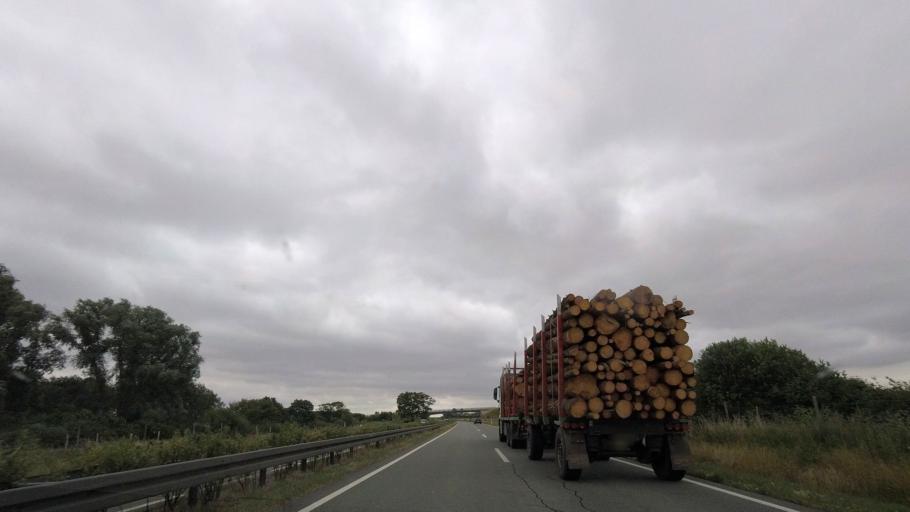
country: DE
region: Mecklenburg-Vorpommern
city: Brandshagen
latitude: 54.1449
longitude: 13.1634
